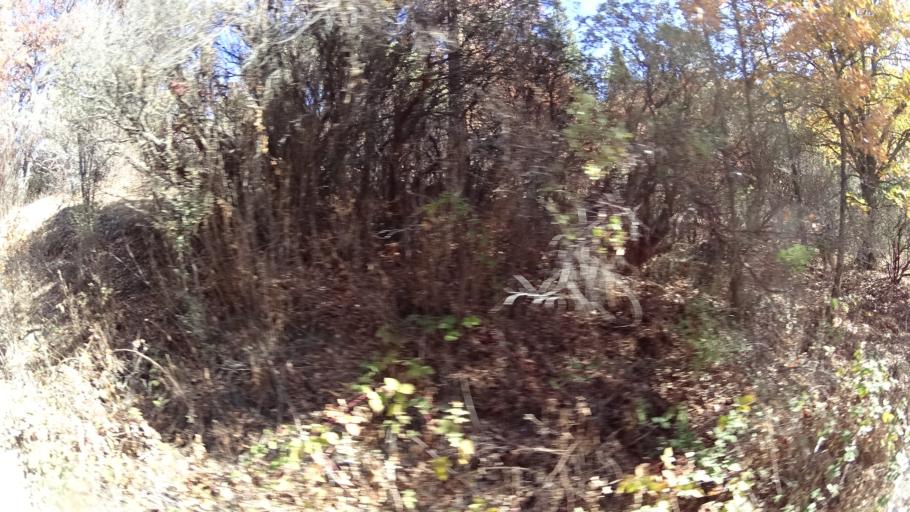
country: US
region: California
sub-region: Siskiyou County
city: Yreka
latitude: 41.8420
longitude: -122.8362
